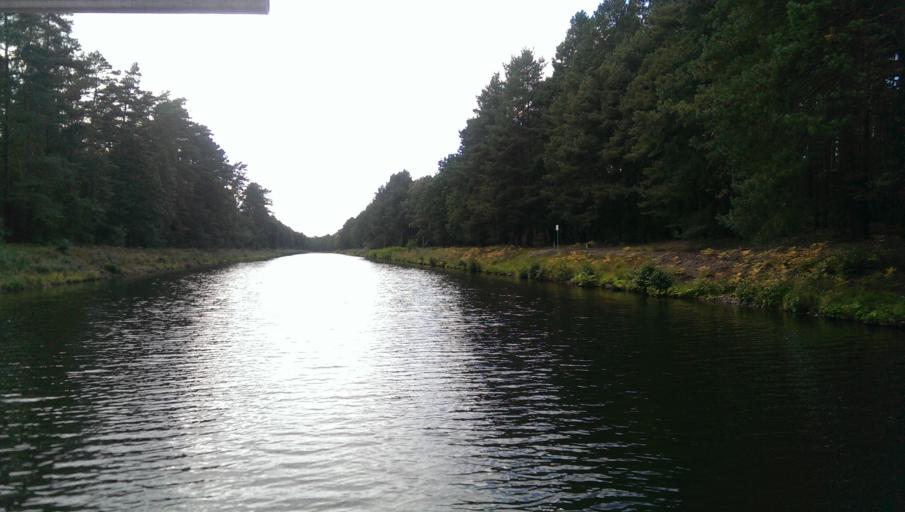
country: DE
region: Brandenburg
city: Liebenwalde
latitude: 52.8470
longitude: 13.4614
